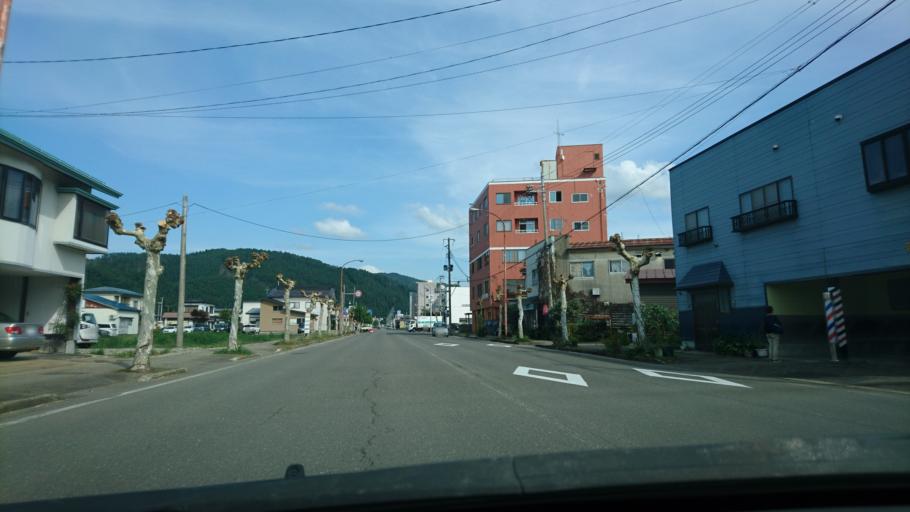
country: JP
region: Akita
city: Yokotemachi
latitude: 39.3089
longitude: 140.5720
